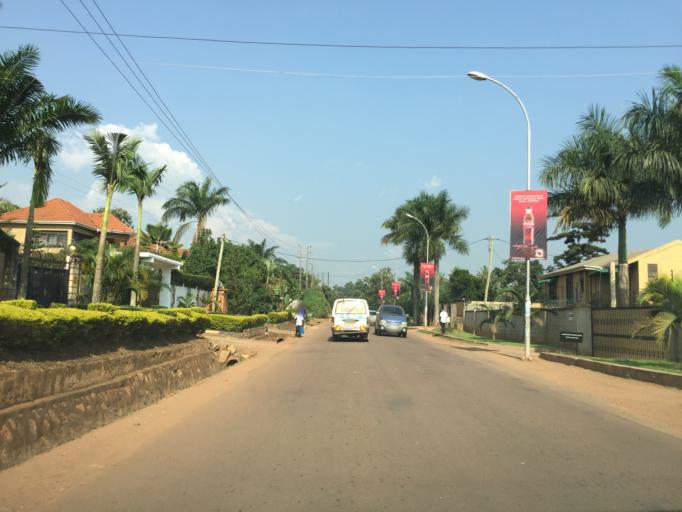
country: UG
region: Central Region
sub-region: Kampala District
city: Kampala
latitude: 0.2394
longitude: 32.6219
